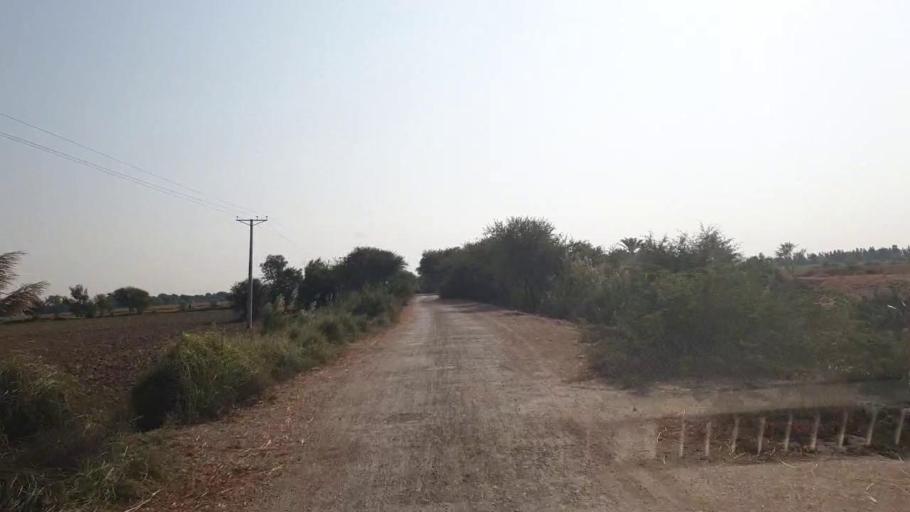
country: PK
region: Sindh
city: Kario
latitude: 24.8979
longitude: 68.6476
